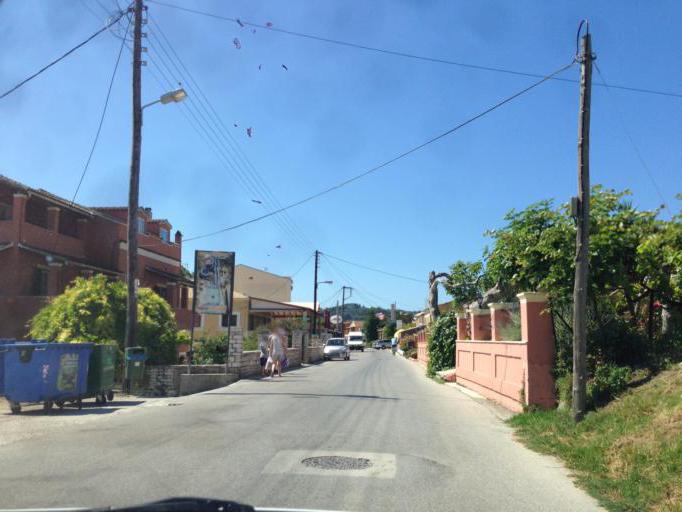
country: GR
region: Ionian Islands
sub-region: Nomos Kerkyras
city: Agios Georgis
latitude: 39.7856
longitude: 19.7081
